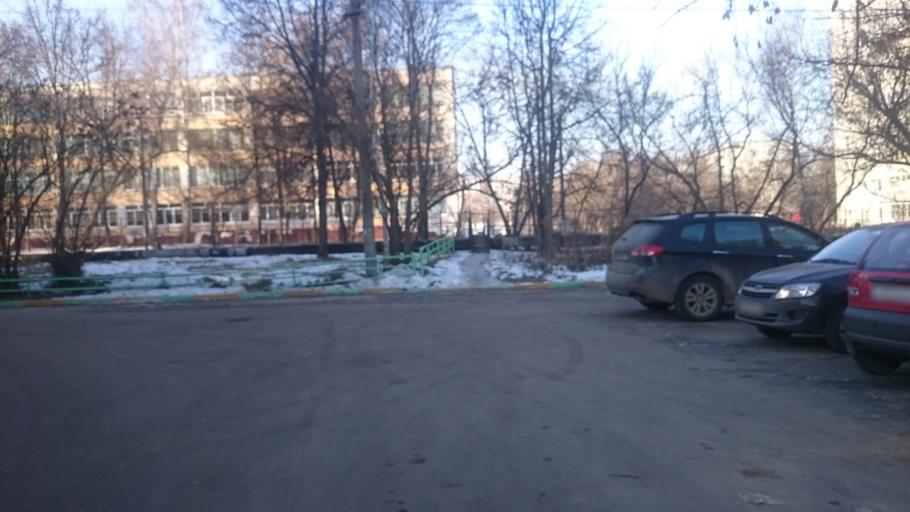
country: RU
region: Tula
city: Tula
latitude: 54.1754
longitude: 37.6395
